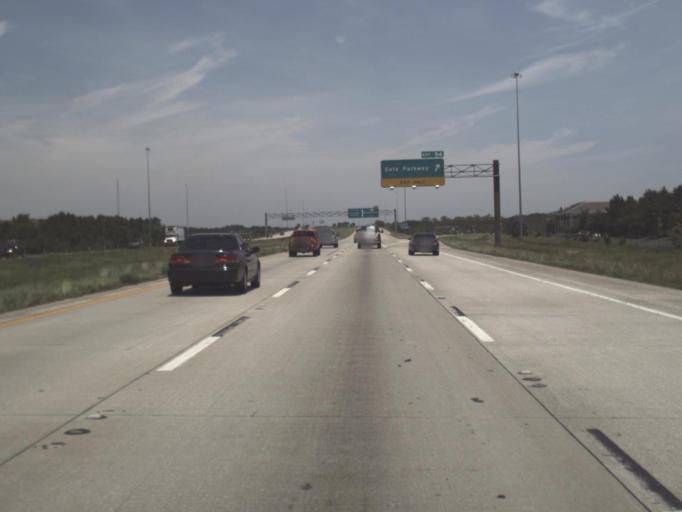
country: US
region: Florida
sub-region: Saint Johns County
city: Ponte Vedra Beach
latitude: 30.2290
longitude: -81.5139
